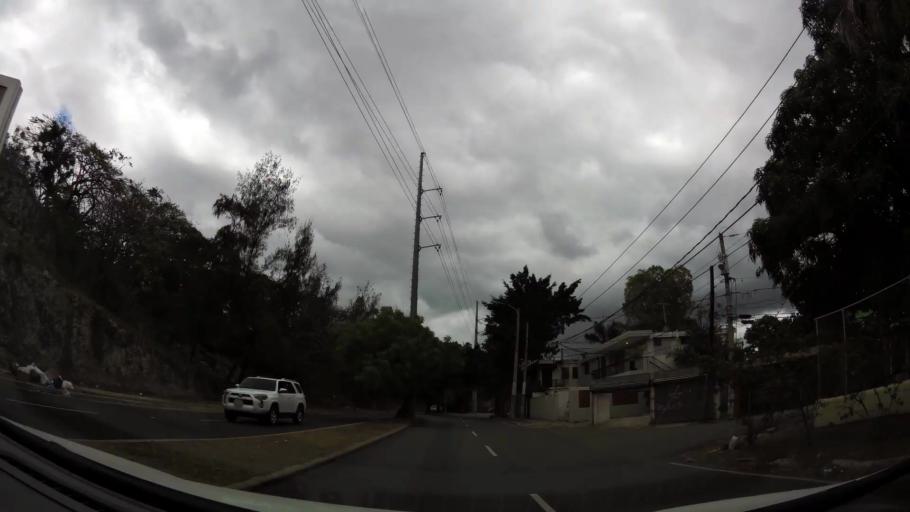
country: DO
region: Nacional
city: Bella Vista
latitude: 18.4471
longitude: -69.9421
